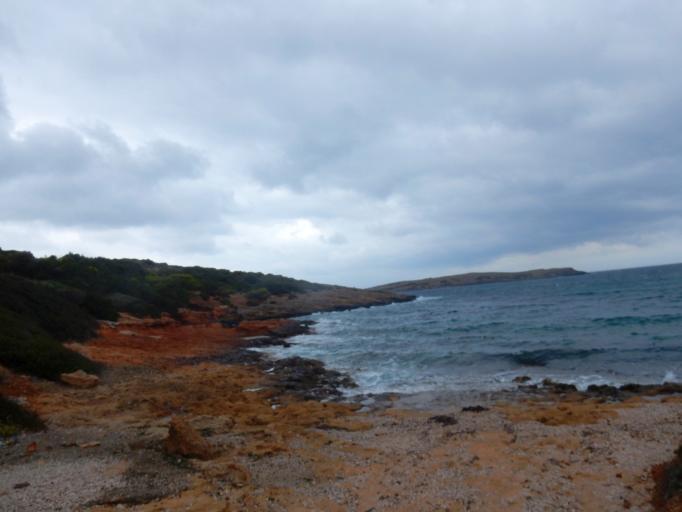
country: GR
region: Attica
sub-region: Nomarchia Anatolikis Attikis
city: Limin Mesoyaias
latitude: 37.9112
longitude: 24.0381
